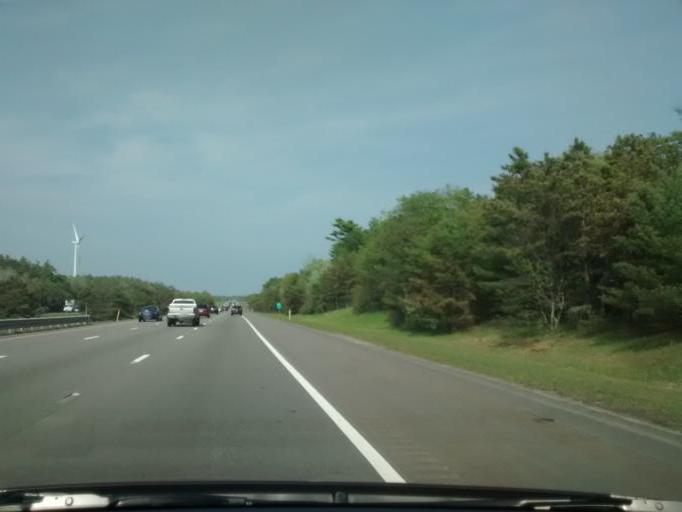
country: US
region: Massachusetts
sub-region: Plymouth County
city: White Island Shores
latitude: 41.7751
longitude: -70.6348
